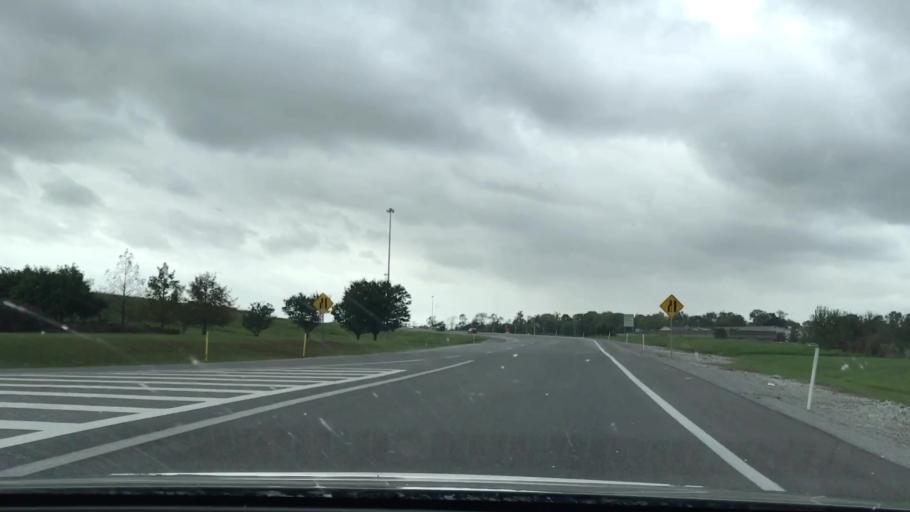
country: US
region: Kentucky
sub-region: Christian County
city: Hopkinsville
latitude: 36.8332
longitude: -87.4742
